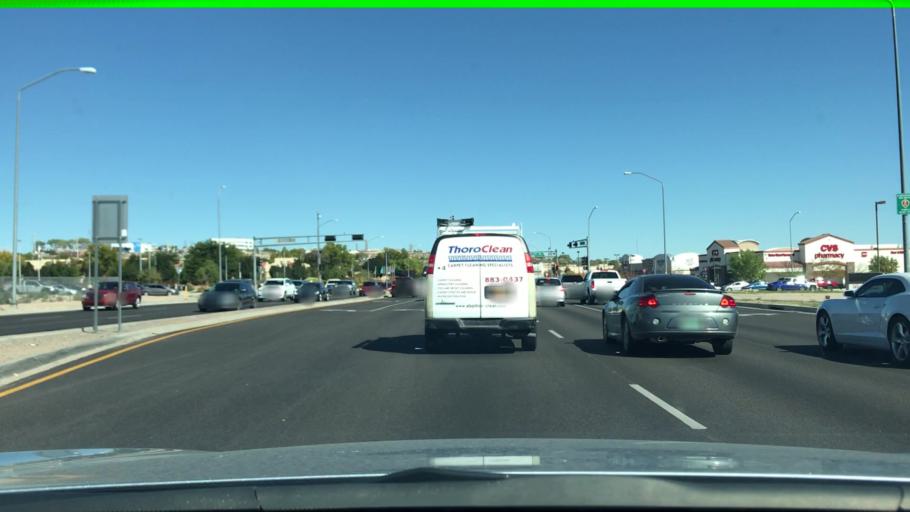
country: US
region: New Mexico
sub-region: Sandoval County
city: Rio Rancho
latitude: 35.2047
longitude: -106.6593
